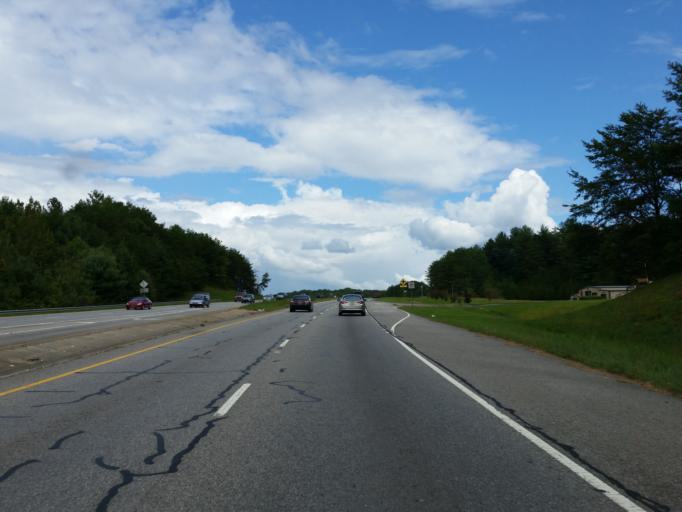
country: US
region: Georgia
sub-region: Fannin County
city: Blue Ridge
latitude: 34.8902
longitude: -84.2844
